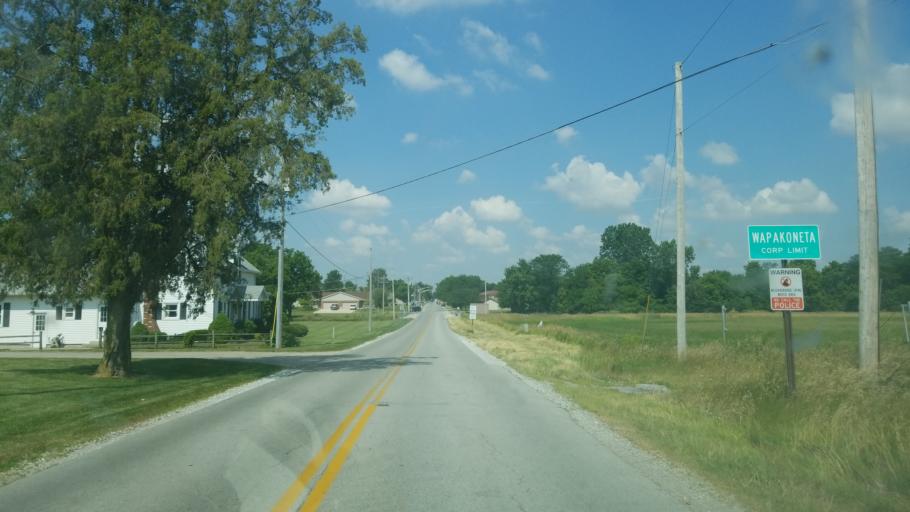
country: US
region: Ohio
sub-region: Auglaize County
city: Wapakoneta
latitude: 40.5701
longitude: -84.1740
